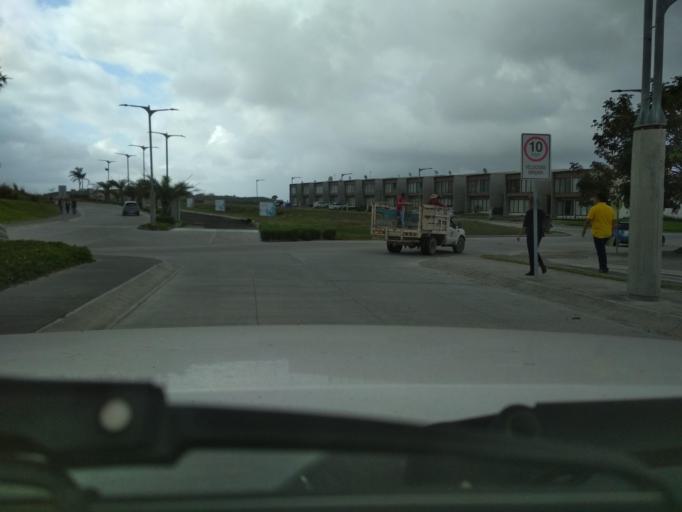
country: MX
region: Veracruz
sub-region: Veracruz
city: Fraccionamiento Geovillas los Pinos
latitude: 19.2171
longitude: -96.2299
